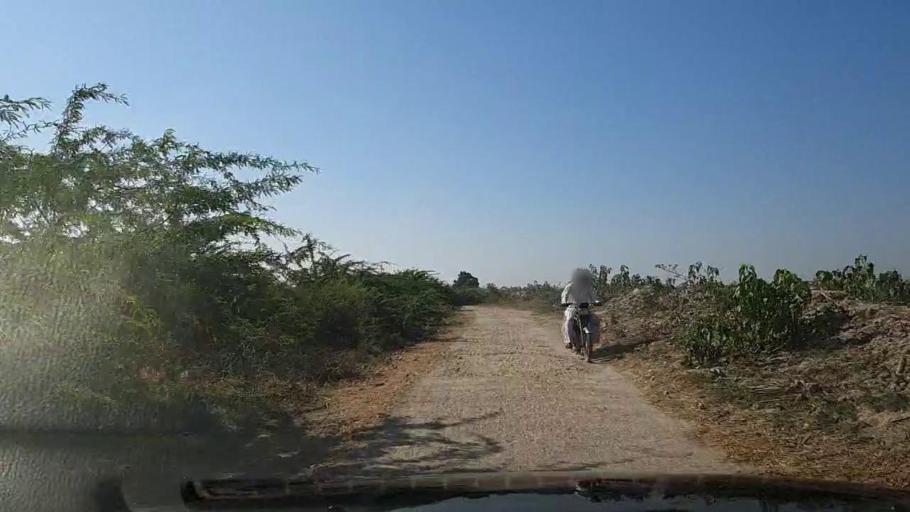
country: PK
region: Sindh
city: Thatta
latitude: 24.7147
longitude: 67.9195
